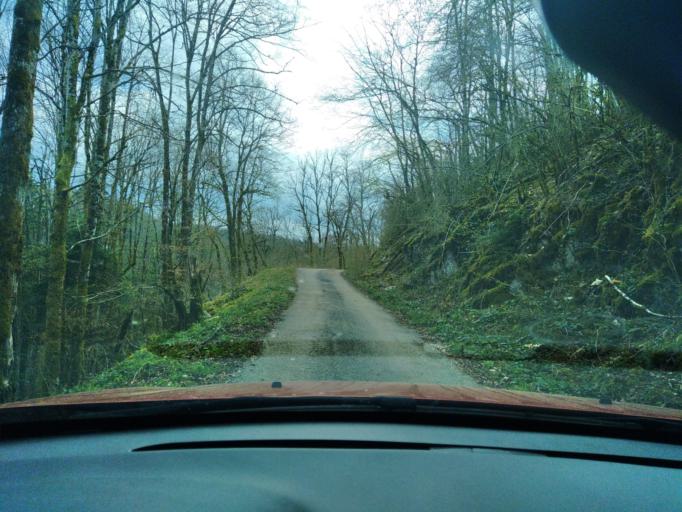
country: FR
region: Franche-Comte
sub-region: Departement du Jura
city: Moirans-en-Montagne
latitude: 46.4702
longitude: 5.7627
